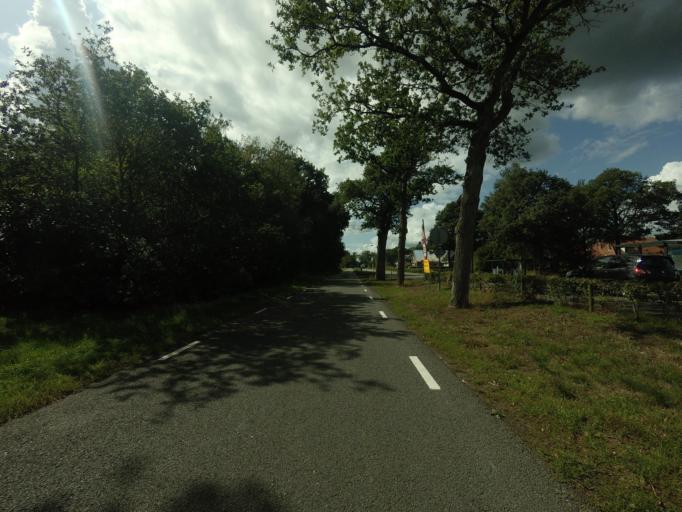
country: NL
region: Friesland
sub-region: Gemeente Heerenveen
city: Jubbega
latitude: 52.9577
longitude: 6.1883
